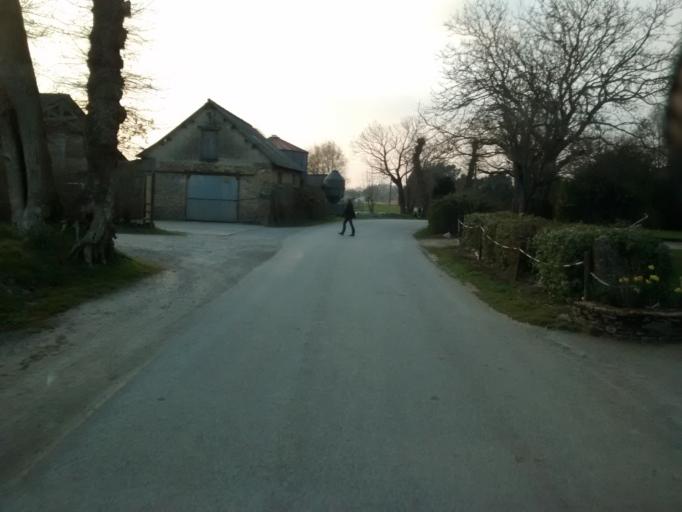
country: FR
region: Brittany
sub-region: Departement du Morbihan
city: Meneac
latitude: 48.1420
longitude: -2.4655
